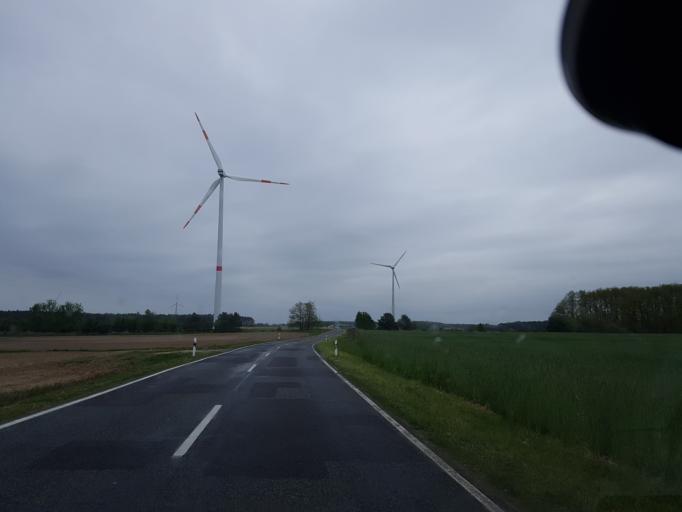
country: DE
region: Brandenburg
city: Drebkau
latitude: 51.6529
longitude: 14.2793
